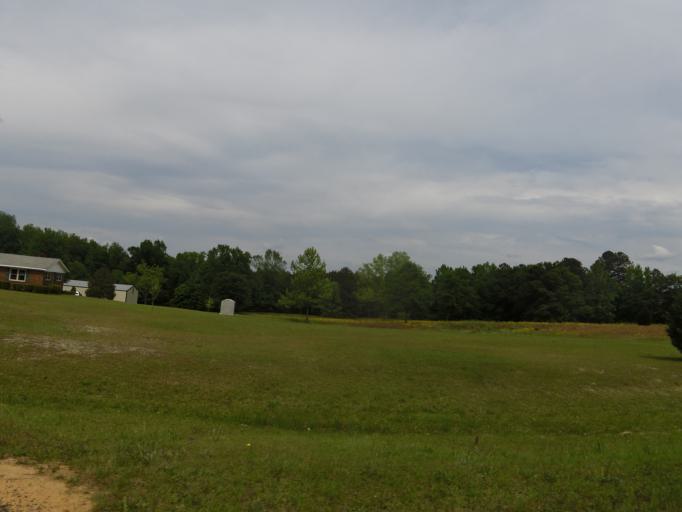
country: US
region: Georgia
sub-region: McDuffie County
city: Thomson
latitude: 33.3654
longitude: -82.4661
